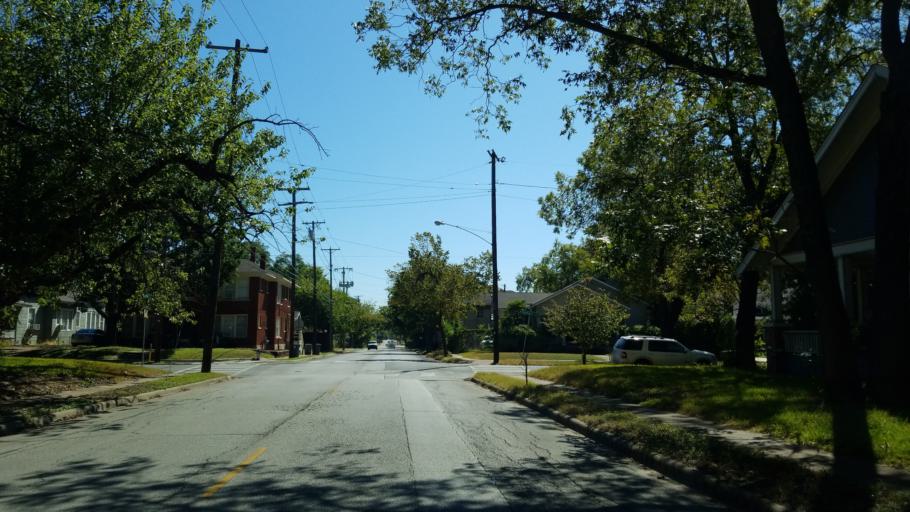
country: US
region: Texas
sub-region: Dallas County
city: Highland Park
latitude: 32.8038
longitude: -96.7594
